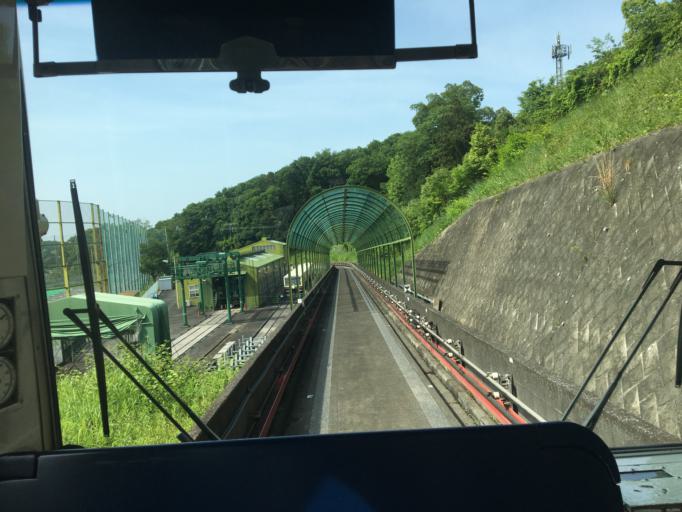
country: JP
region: Tokyo
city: Higashimurayama-shi
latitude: 35.7701
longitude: 139.4221
